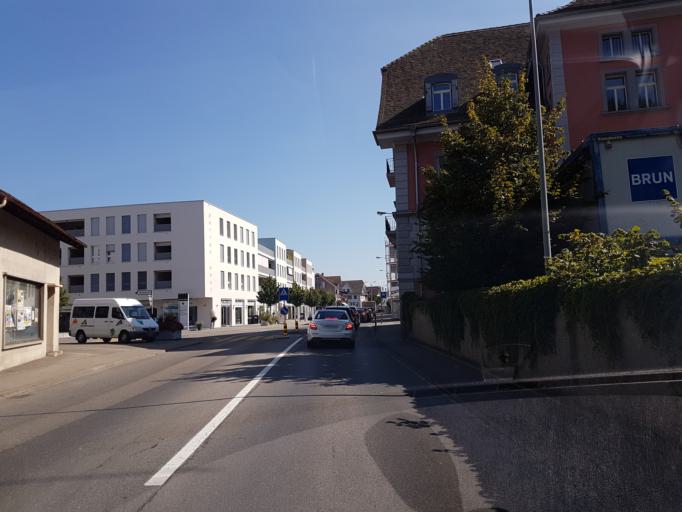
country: CH
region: Aargau
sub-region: Bezirk Muri
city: Muri
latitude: 47.2751
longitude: 8.3404
